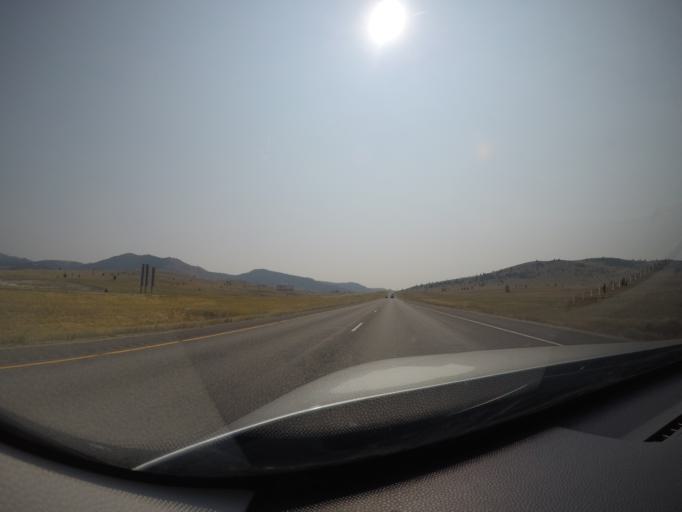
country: US
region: Montana
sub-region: Deer Lodge County
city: Warm Springs
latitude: 46.0512
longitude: -112.7534
